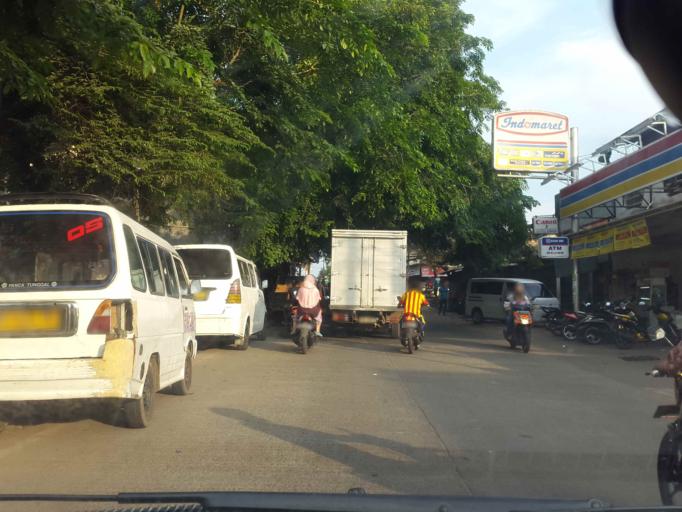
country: ID
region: Banten
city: South Tangerang
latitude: -6.2623
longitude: 106.7218
